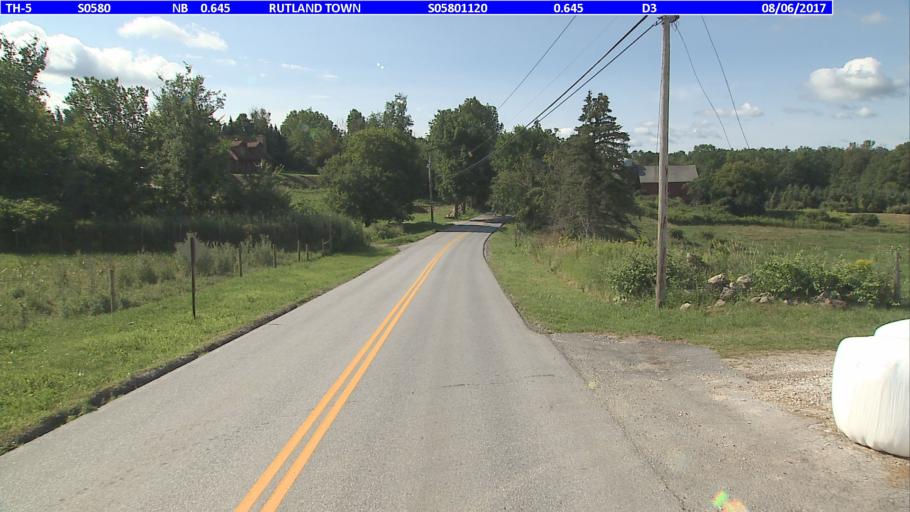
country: US
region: Vermont
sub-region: Rutland County
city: Rutland
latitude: 43.5768
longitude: -72.9515
